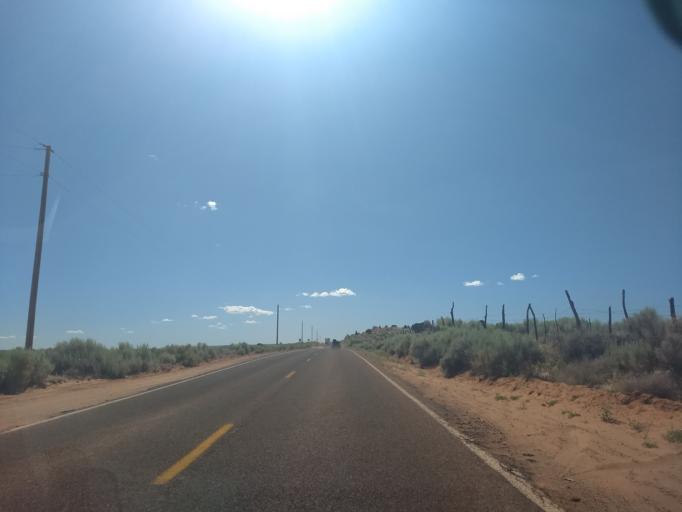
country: US
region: Arizona
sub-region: Mohave County
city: Colorado City
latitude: 36.9469
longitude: -112.9174
